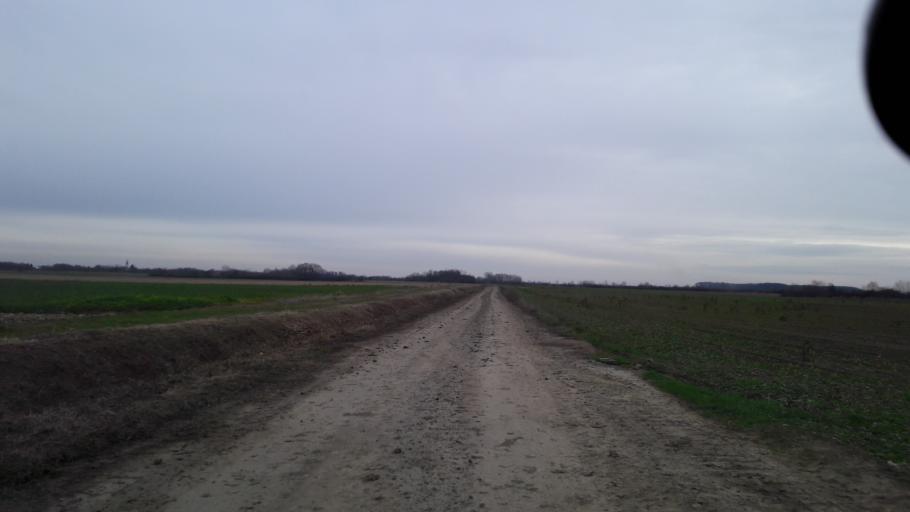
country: HR
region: Osjecko-Baranjska
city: Vladislavci
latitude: 45.4264
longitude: 18.5761
